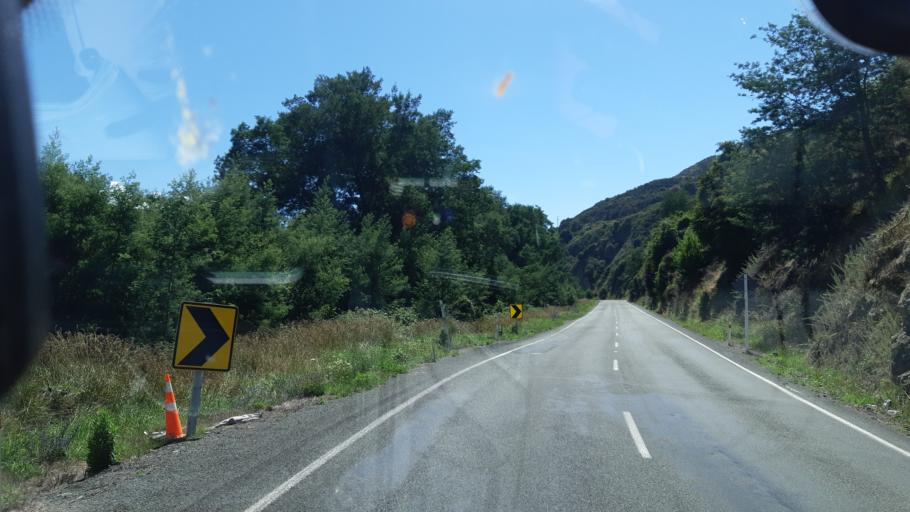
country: NZ
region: Canterbury
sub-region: Kaikoura District
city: Kaikoura
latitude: -42.6334
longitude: 173.3513
